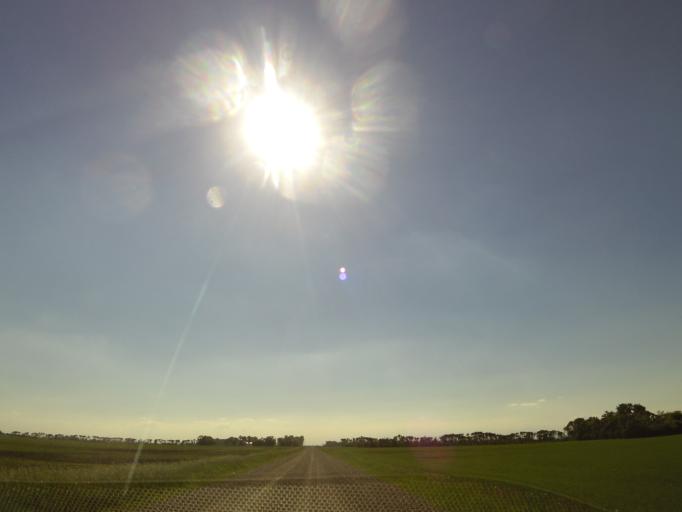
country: US
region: North Dakota
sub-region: Walsh County
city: Grafton
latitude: 48.3535
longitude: -97.2450
